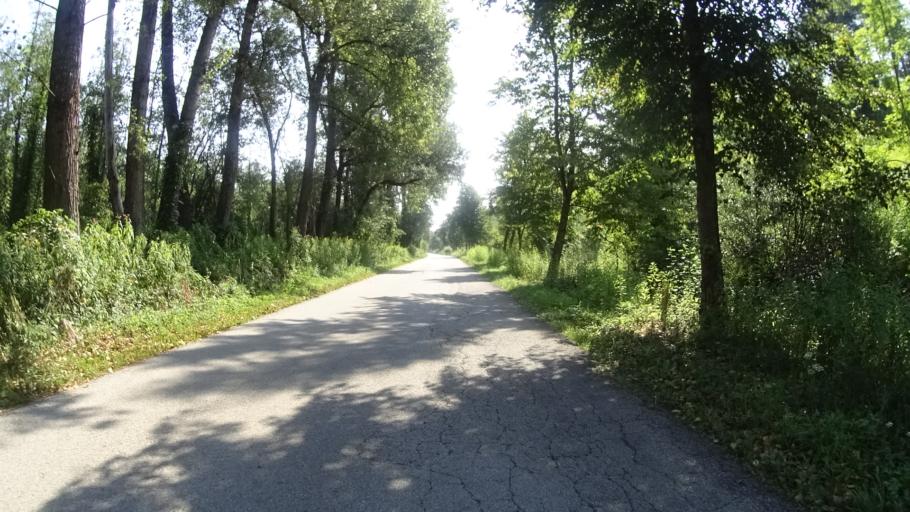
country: AT
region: Carinthia
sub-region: Politischer Bezirk Klagenfurt Land
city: Grafenstein
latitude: 46.5596
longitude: 14.4351
